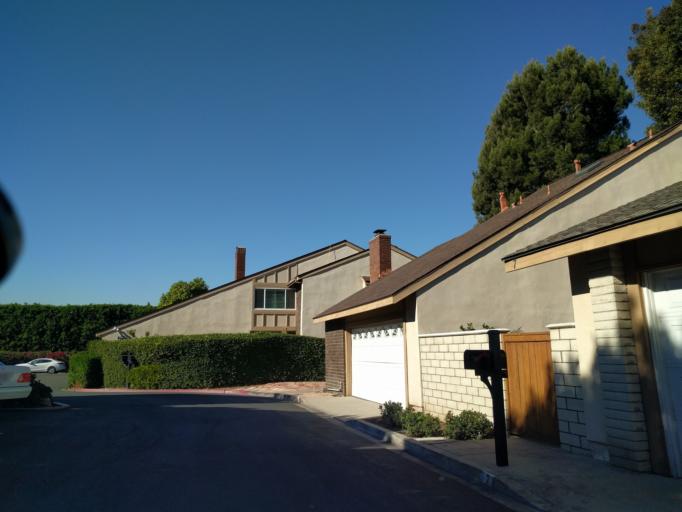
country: US
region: California
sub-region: Orange County
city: Irvine
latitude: 33.7053
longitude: -117.7833
